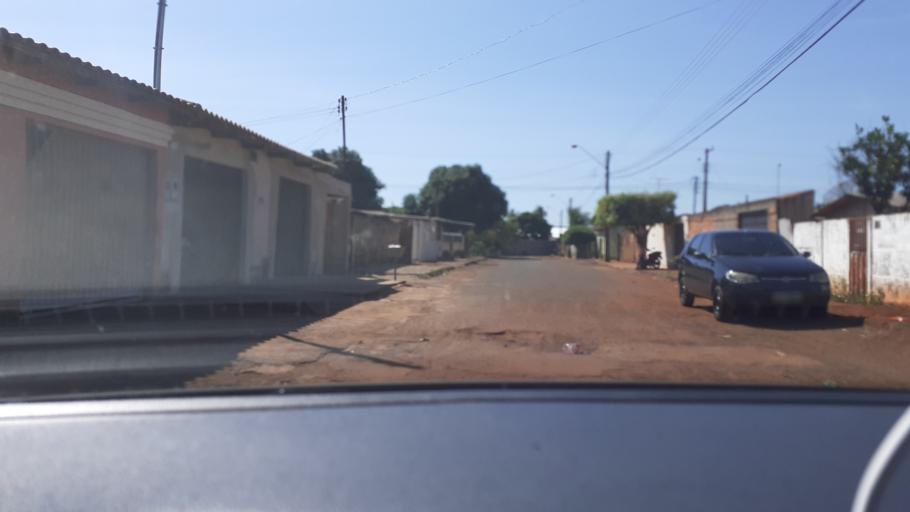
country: BR
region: Goias
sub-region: Itumbiara
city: Itumbiara
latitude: -18.4117
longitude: -49.2545
